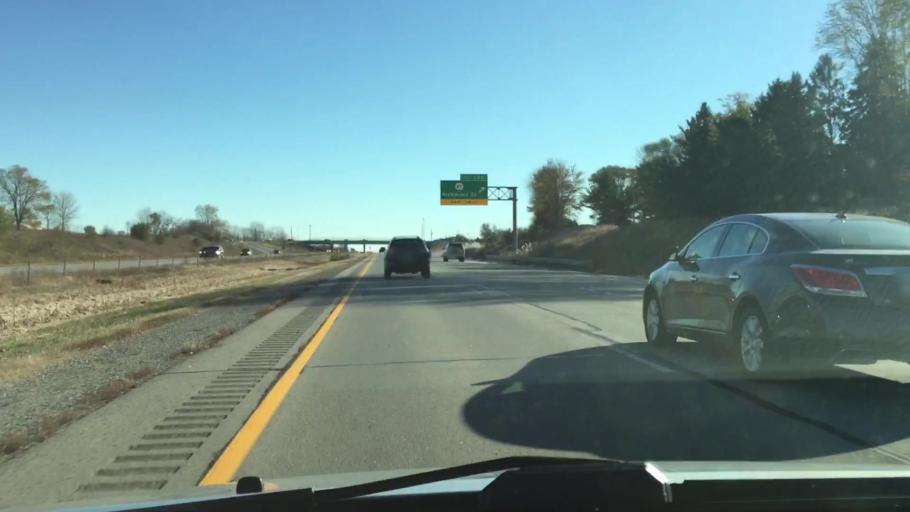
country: US
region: Wisconsin
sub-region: Outagamie County
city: Appleton
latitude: 44.2986
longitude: -88.4228
